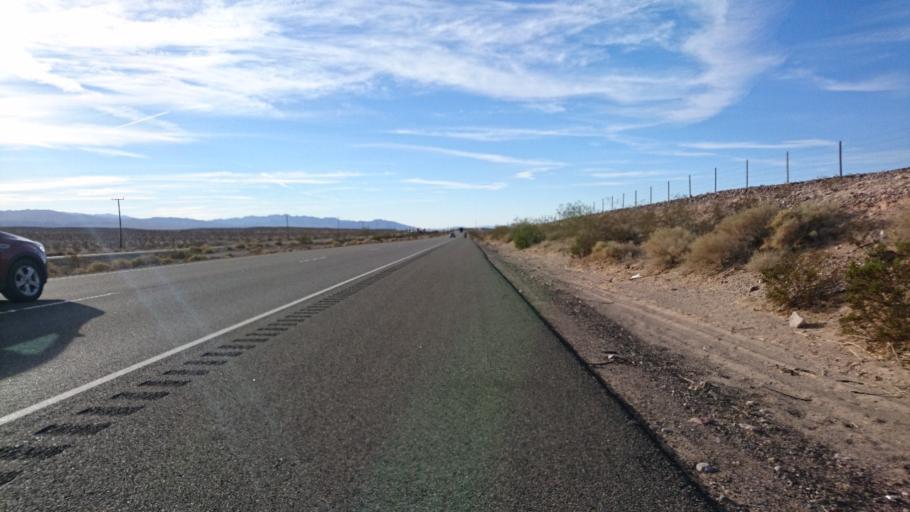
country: US
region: California
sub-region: San Bernardino County
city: Fort Irwin
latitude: 34.7824
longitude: -116.4097
